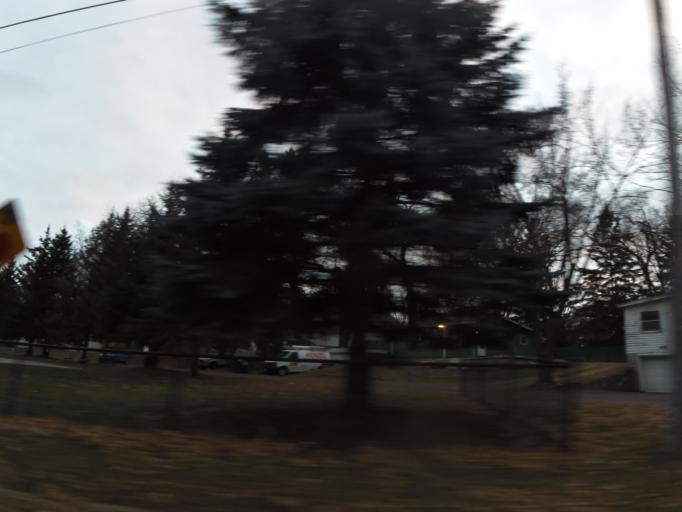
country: US
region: Minnesota
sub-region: Washington County
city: Mahtomedi
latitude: 45.0570
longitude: -92.9564
